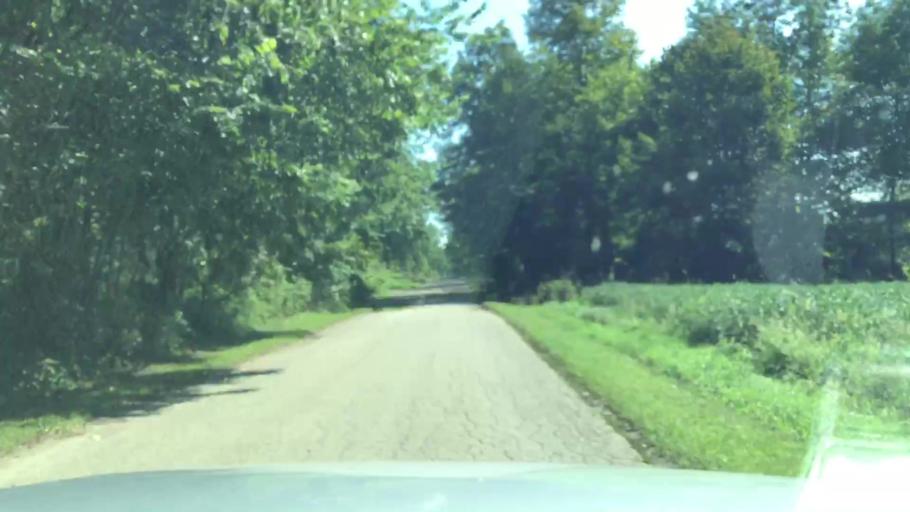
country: US
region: Michigan
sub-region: Lenawee County
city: Manitou Beach-Devils Lake
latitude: 41.9935
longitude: -84.3407
